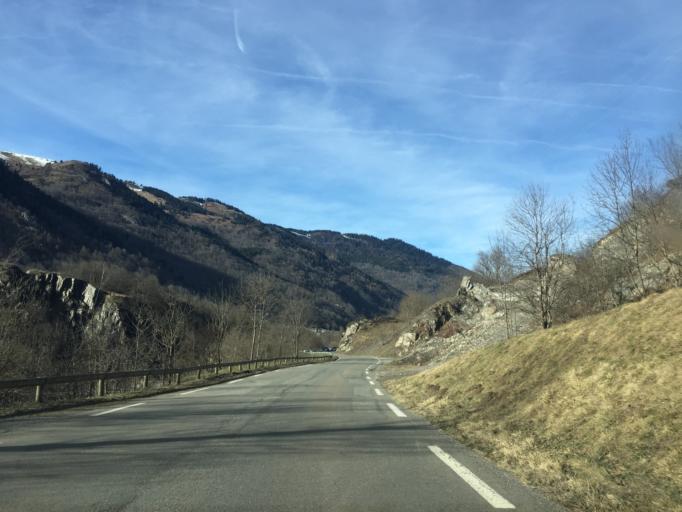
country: FR
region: Midi-Pyrenees
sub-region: Departement des Hautes-Pyrenees
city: Saint-Lary-Soulan
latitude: 42.8084
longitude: 0.4104
